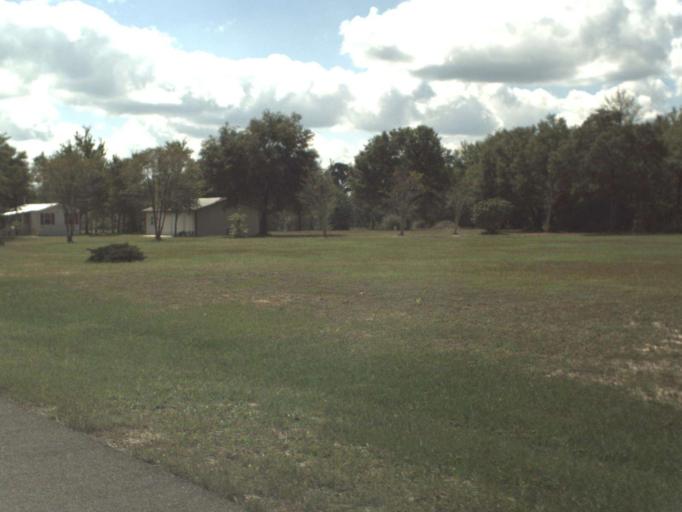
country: US
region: Florida
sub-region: Walton County
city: Freeport
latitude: 30.5632
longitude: -85.9203
